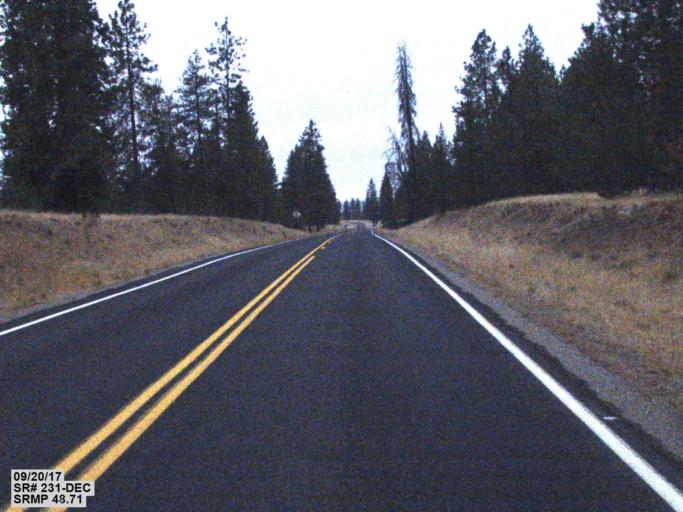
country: US
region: Washington
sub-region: Spokane County
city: Fairchild Air Force Base
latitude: 47.8903
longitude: -117.8298
